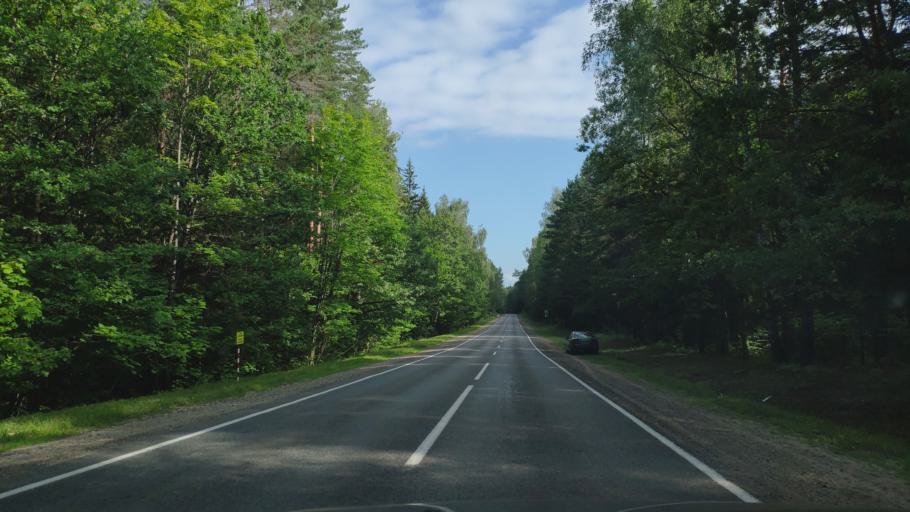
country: BY
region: Minsk
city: Novosel'ye
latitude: 53.9469
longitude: 27.2454
